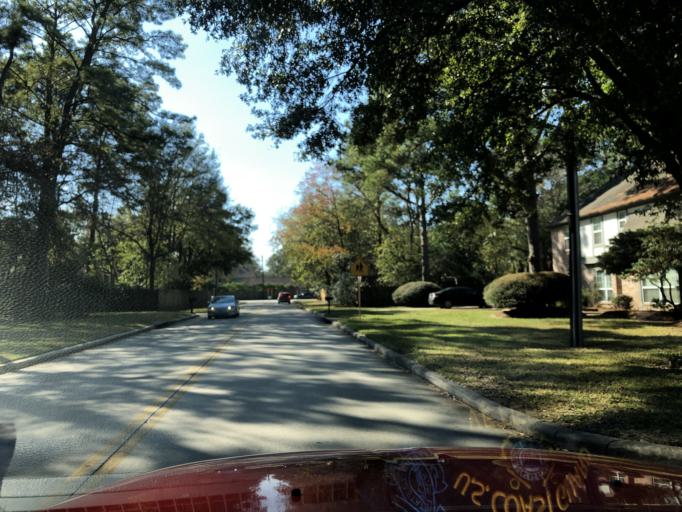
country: US
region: Texas
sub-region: Harris County
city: Tomball
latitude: 30.0271
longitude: -95.5410
